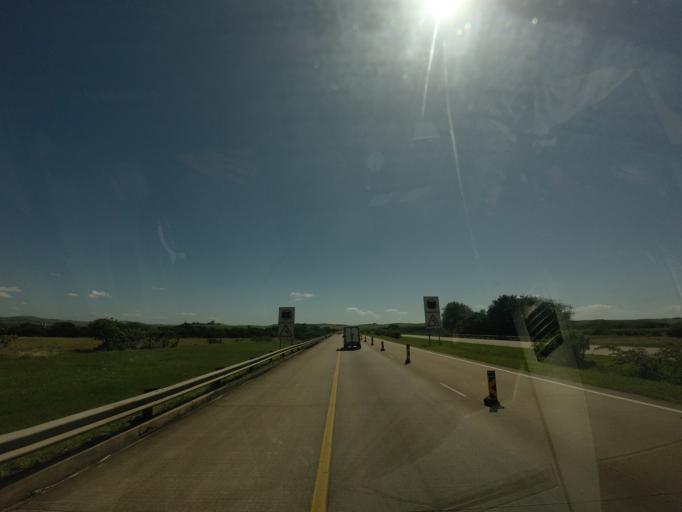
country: ZA
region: KwaZulu-Natal
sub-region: iLembe District Municipality
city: Stanger
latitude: -29.3731
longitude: 31.3007
